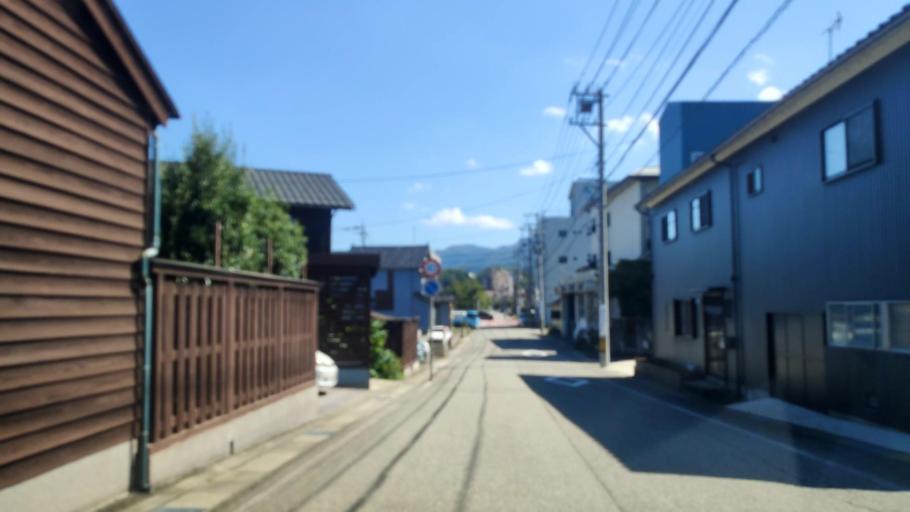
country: JP
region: Ishikawa
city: Nanao
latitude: 37.3898
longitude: 136.9010
